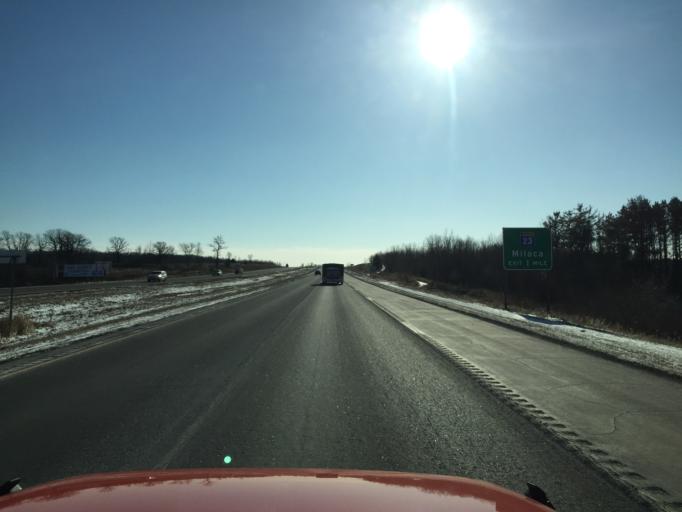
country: US
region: Minnesota
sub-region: Mille Lacs County
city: Milaca
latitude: 45.7767
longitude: -93.6479
